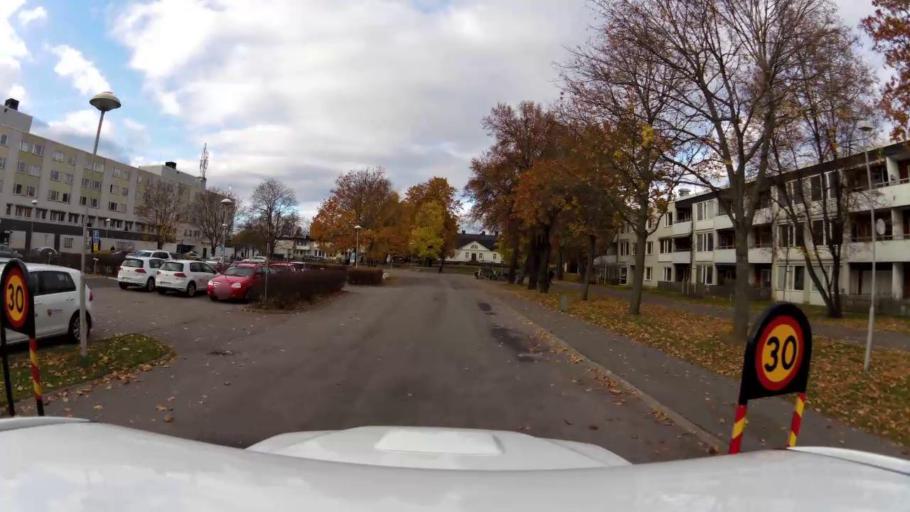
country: SE
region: OEstergoetland
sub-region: Linkopings Kommun
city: Malmslatt
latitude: 58.4086
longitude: 15.5643
